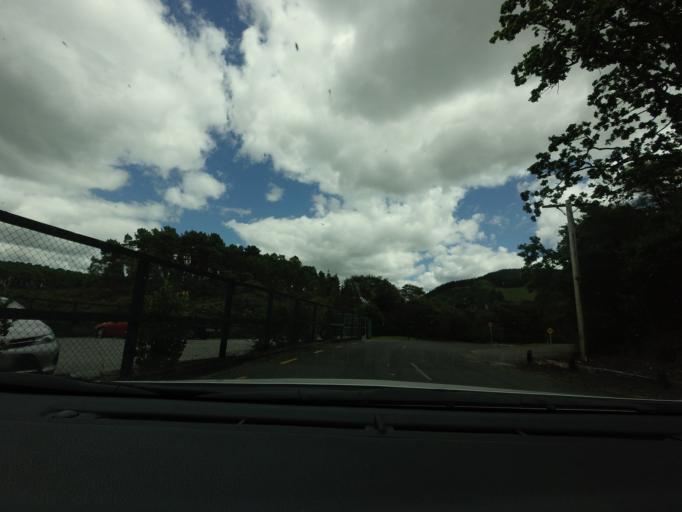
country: NZ
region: Bay of Plenty
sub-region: Rotorua District
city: Rotorua
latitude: -38.3558
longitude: 176.3671
